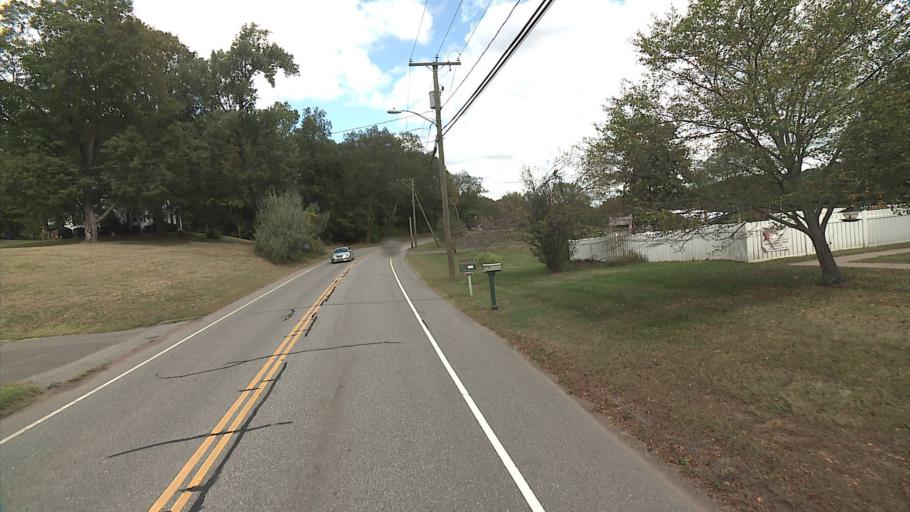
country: US
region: Connecticut
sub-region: Middlesex County
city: Durham
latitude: 41.5188
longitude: -72.7099
